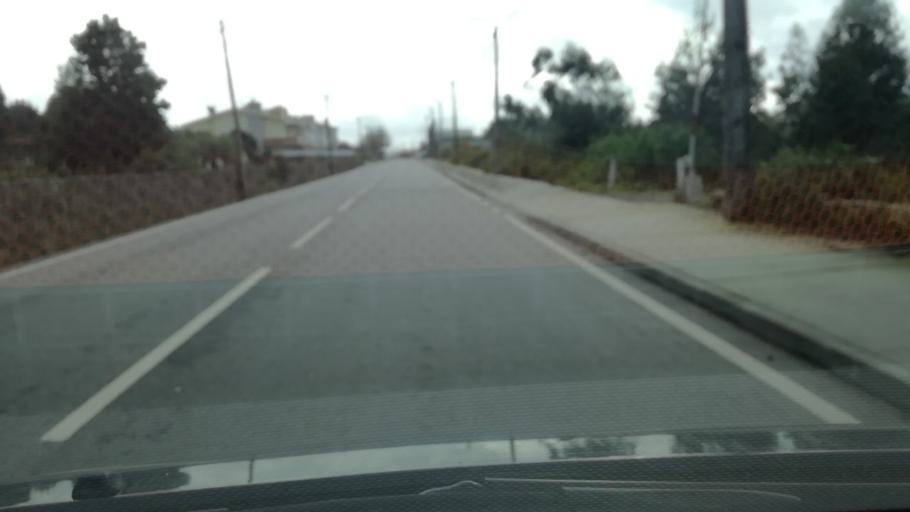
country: PT
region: Porto
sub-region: Maia
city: Anta
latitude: 41.2506
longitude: -8.6377
